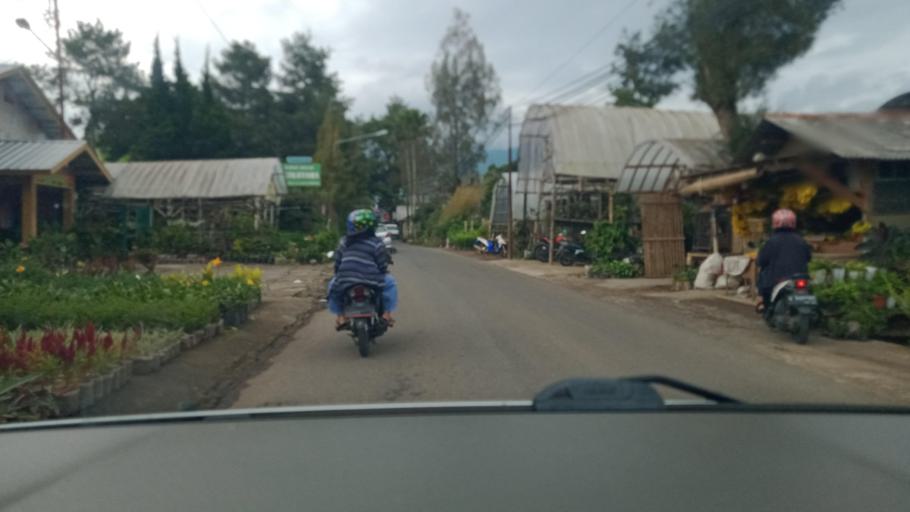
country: ID
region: West Java
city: Lembang
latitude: -6.8194
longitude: 107.5948
